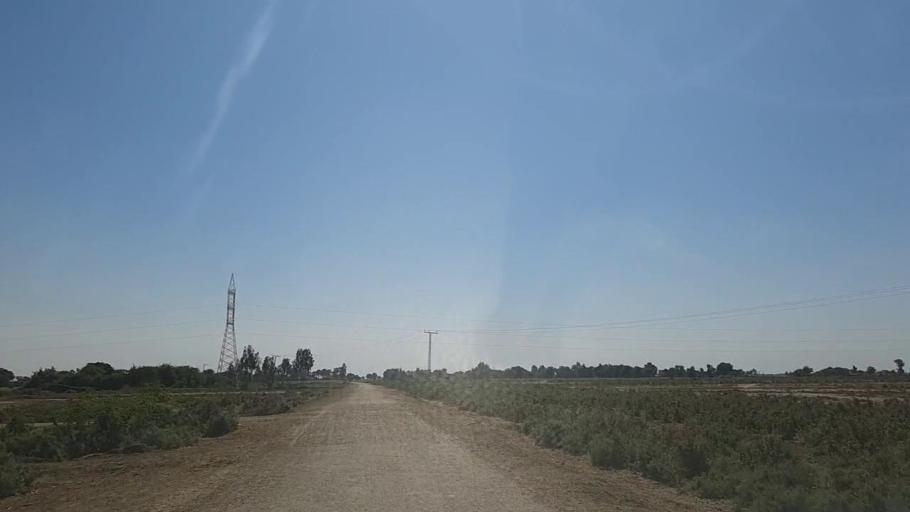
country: PK
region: Sindh
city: Samaro
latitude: 25.2972
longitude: 69.5028
